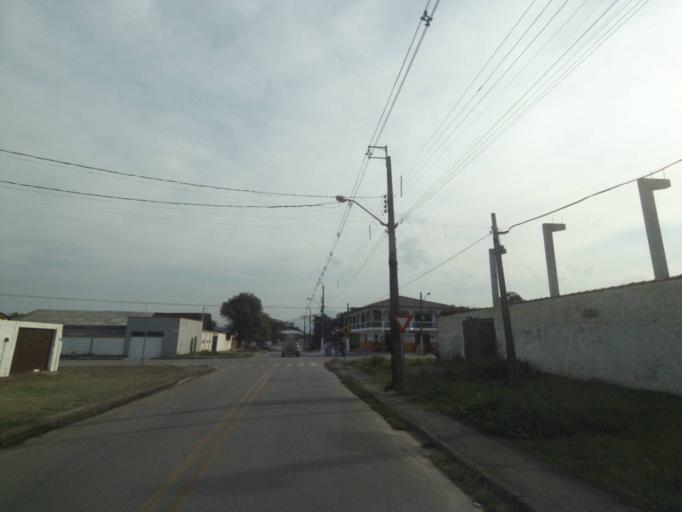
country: BR
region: Parana
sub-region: Paranagua
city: Paranagua
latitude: -25.5241
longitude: -48.5349
